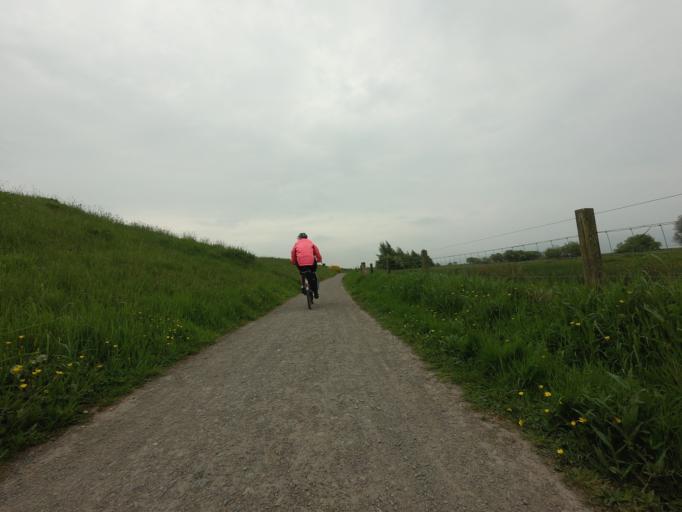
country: GB
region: Scotland
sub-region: Perth and Kinross
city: Milnathort
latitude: 56.2179
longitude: -3.3703
